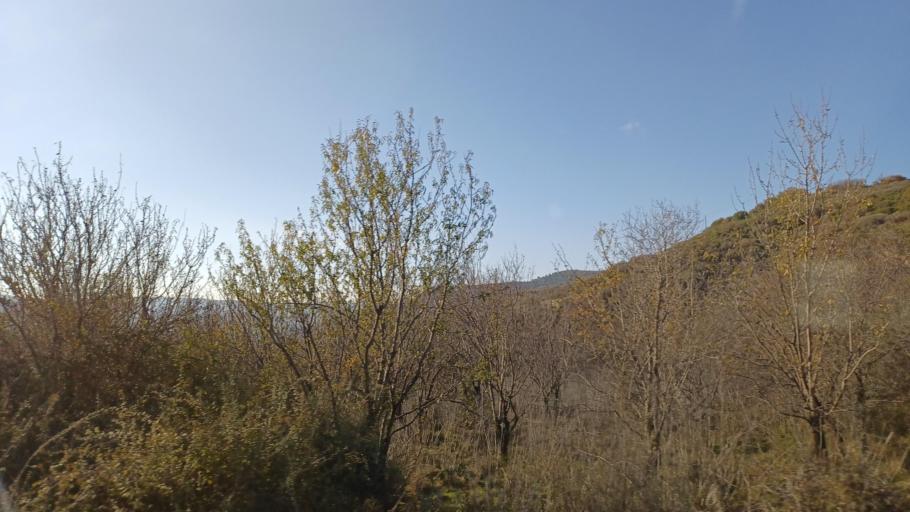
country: CY
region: Limassol
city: Pachna
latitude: 34.8545
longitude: 32.7216
